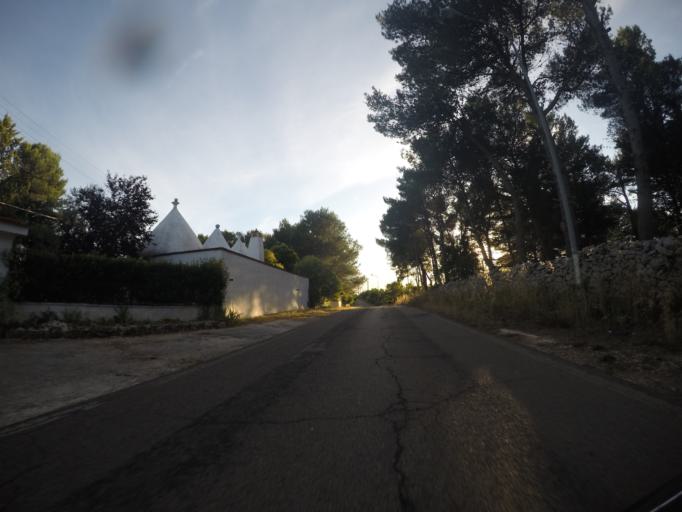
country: IT
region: Apulia
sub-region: Provincia di Taranto
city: Martina Franca
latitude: 40.6542
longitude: 17.3457
